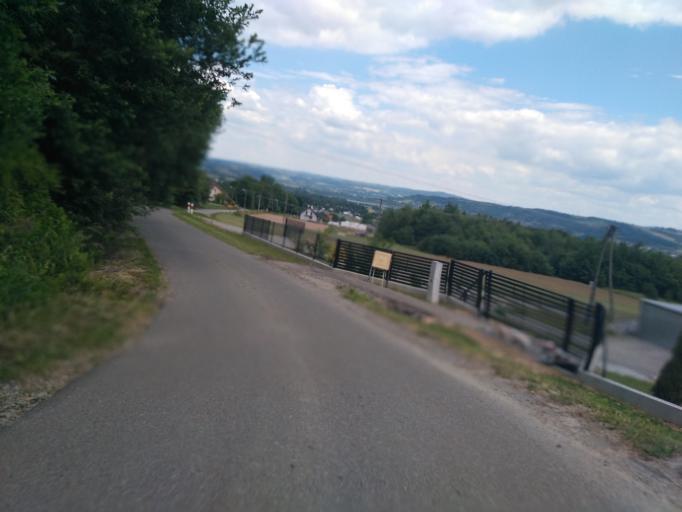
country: PL
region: Subcarpathian Voivodeship
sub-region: Powiat jasielski
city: Brzyska
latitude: 49.8061
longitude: 21.3850
